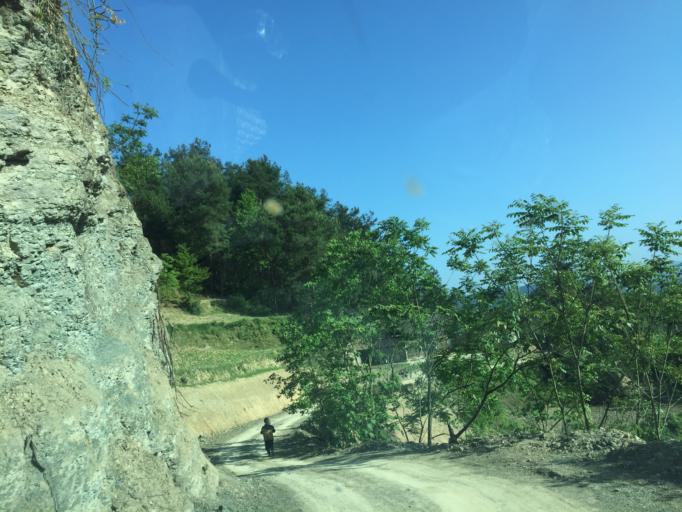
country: CN
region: Guizhou Sheng
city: Xujiaba
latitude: 27.7246
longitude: 108.0247
